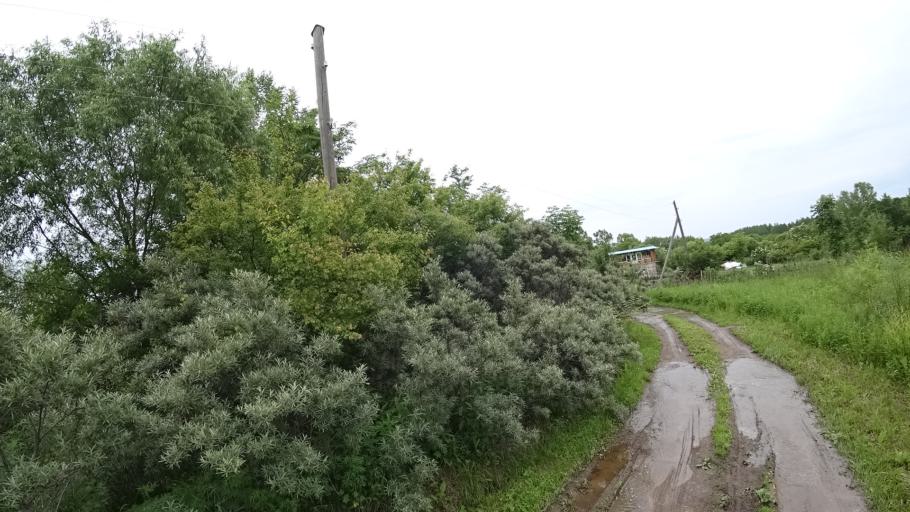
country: RU
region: Primorskiy
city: Novosysoyevka
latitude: 44.2044
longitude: 133.3279
